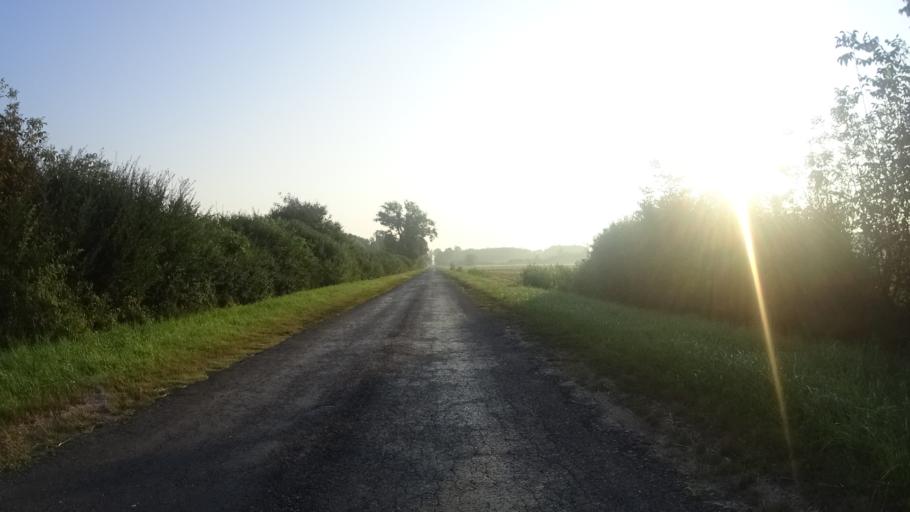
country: HU
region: Zala
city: Zalakomar
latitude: 46.5393
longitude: 17.1524
